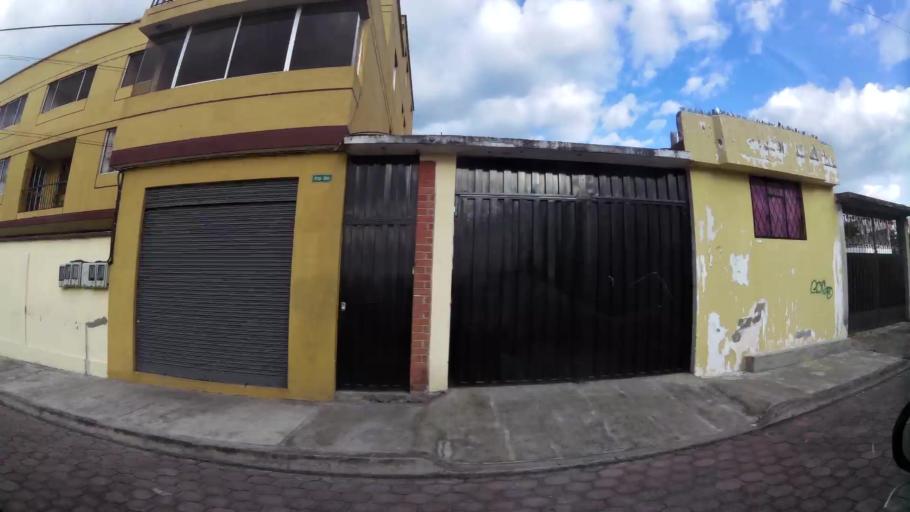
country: EC
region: Pichincha
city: Quito
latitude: -0.1325
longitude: -78.4641
